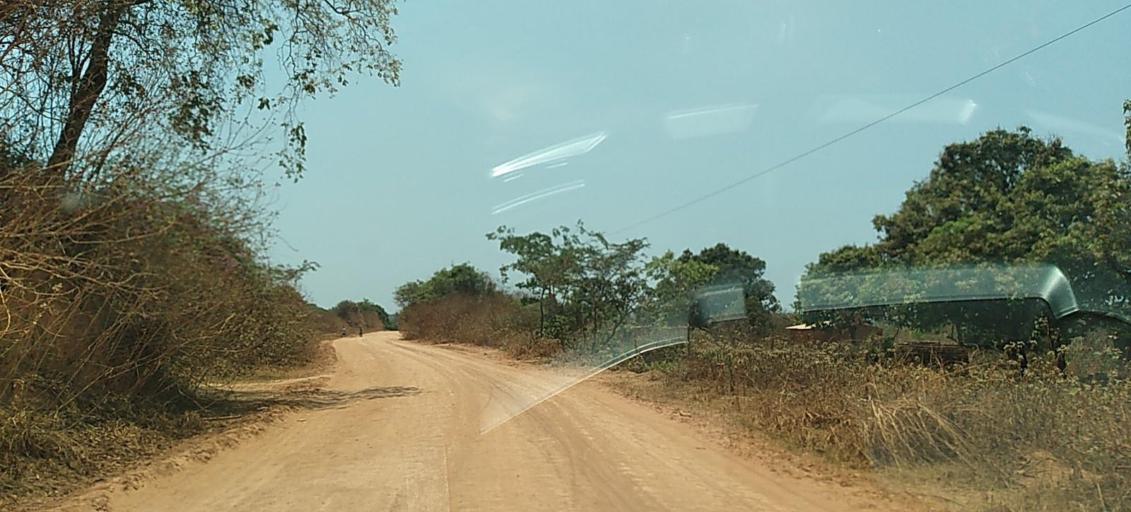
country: CD
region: Katanga
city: Kipushi
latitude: -11.7811
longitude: 27.1850
